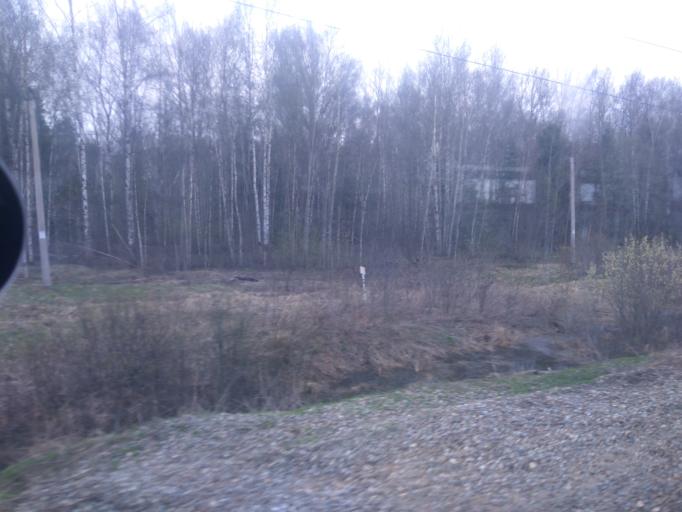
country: RU
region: Moskovskaya
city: Skoropuskovskiy
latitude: 56.3530
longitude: 38.1534
